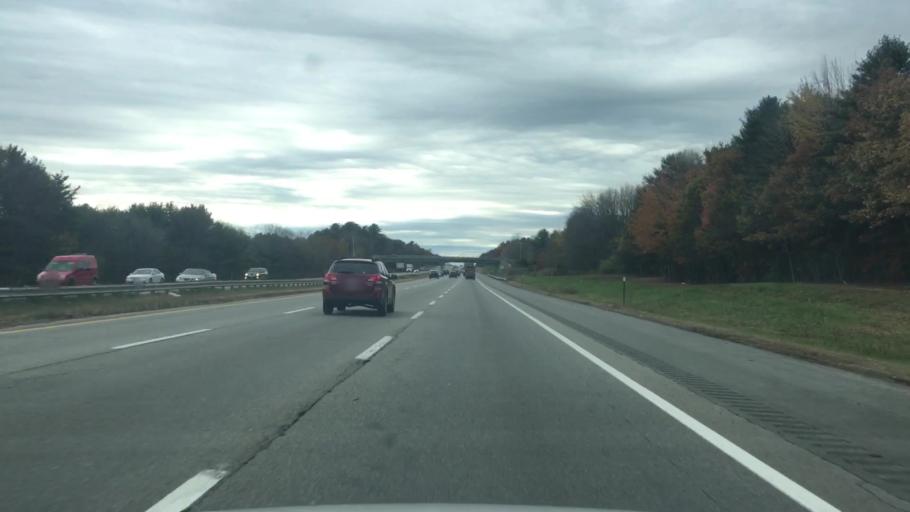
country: US
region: Maine
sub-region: Cumberland County
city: West Scarborough
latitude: 43.5775
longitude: -70.4003
